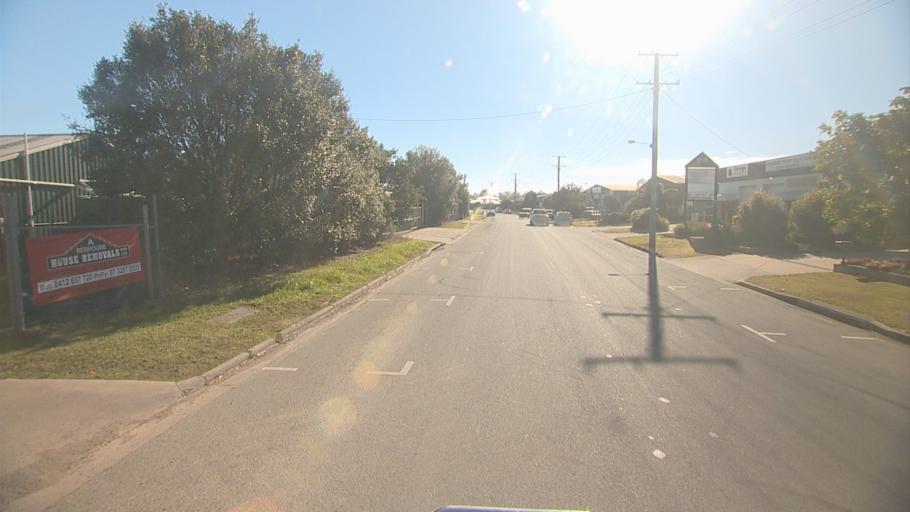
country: AU
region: Queensland
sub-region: Logan
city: Chambers Flat
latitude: -27.7679
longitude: 153.1100
